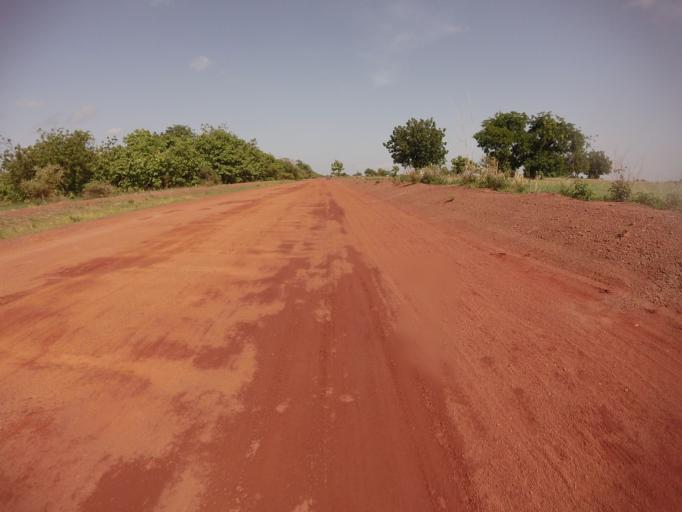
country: GH
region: Upper East
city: Bawku
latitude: 11.0045
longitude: -0.1989
